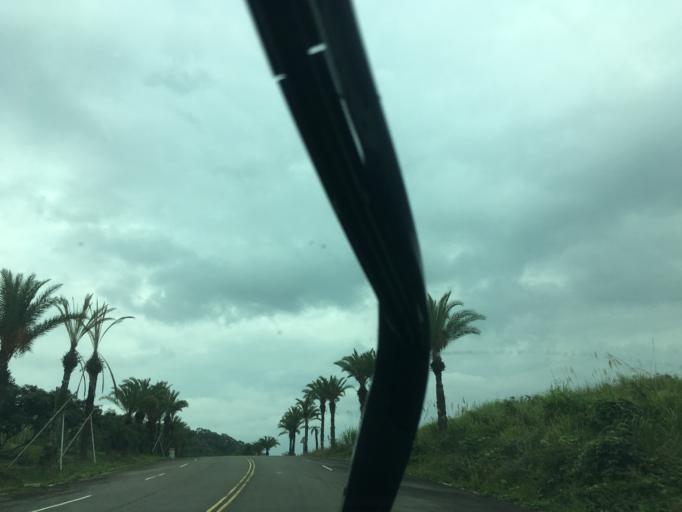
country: TW
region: Taiwan
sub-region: Taichung City
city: Taichung
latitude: 24.0578
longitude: 120.7240
